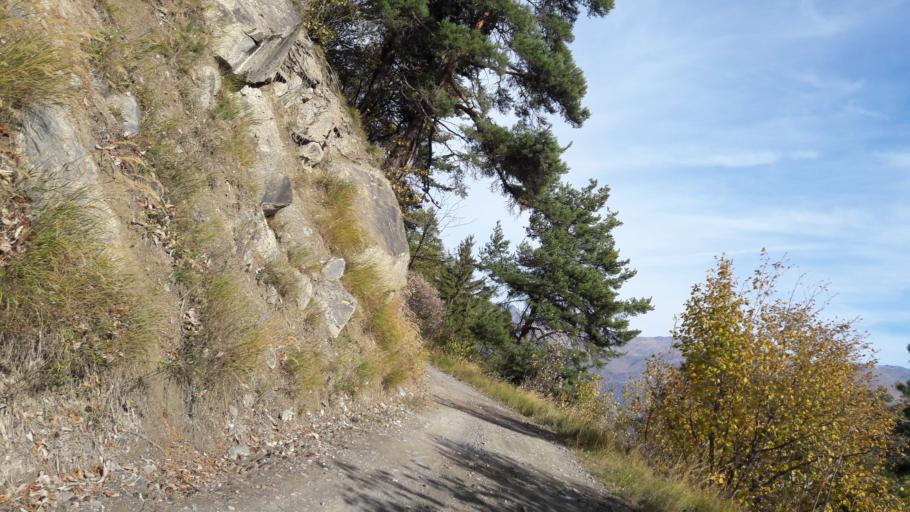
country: FR
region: Rhone-Alpes
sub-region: Departement de la Savoie
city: Valloire
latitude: 45.1913
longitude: 6.4288
